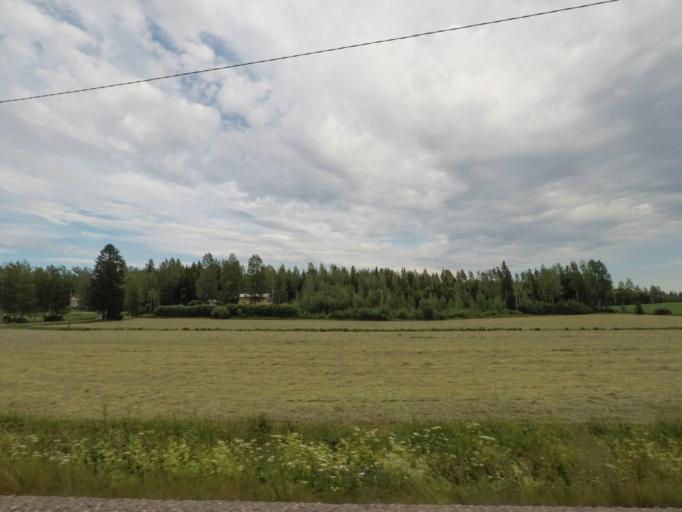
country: FI
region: Uusimaa
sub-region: Porvoo
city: Pukkila
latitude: 60.7752
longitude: 25.4533
